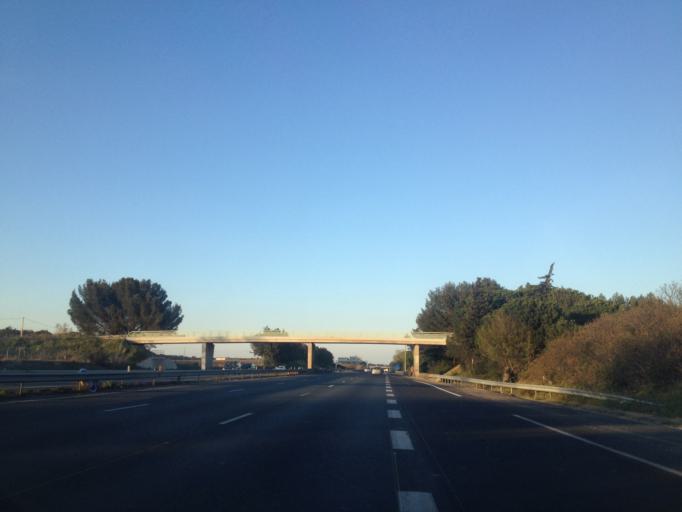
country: FR
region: Languedoc-Roussillon
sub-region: Departement de l'Herault
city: Le Cres
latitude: 43.6096
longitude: 3.9382
